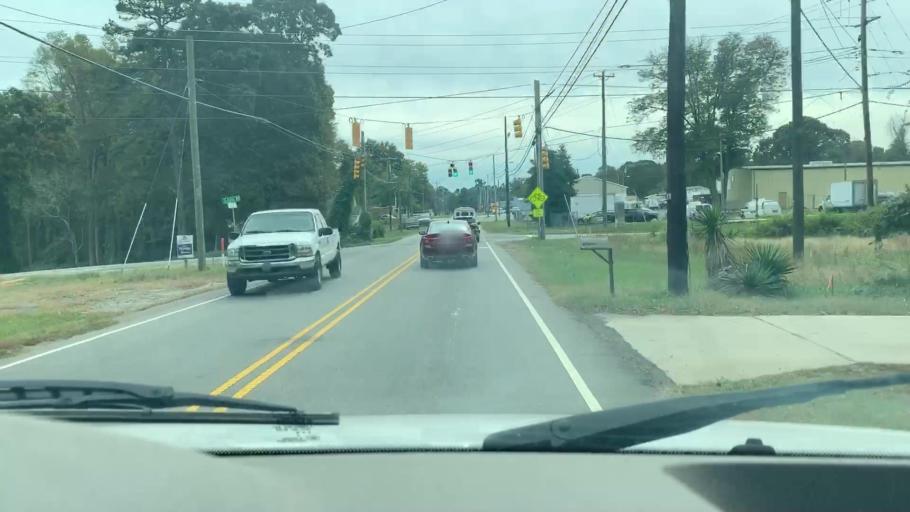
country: US
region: North Carolina
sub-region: Gaston County
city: Davidson
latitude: 35.5436
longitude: -80.8471
